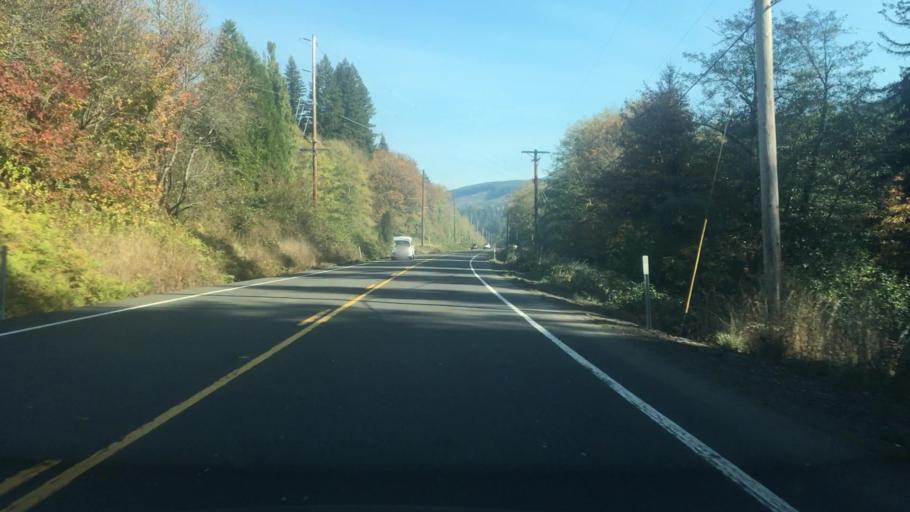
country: US
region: Oregon
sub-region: Lincoln County
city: Rose Lodge
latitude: 45.0217
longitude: -123.8463
